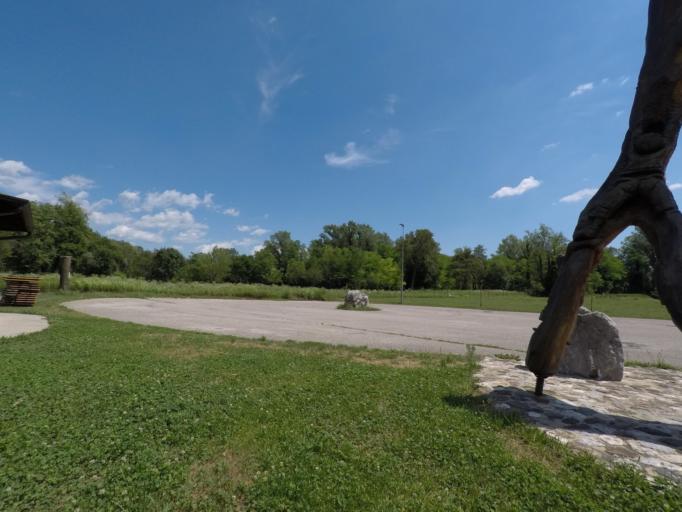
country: IT
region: Friuli Venezia Giulia
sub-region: Provincia di Udine
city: Forgaria nel Friuli
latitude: 46.2252
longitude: 13.0202
